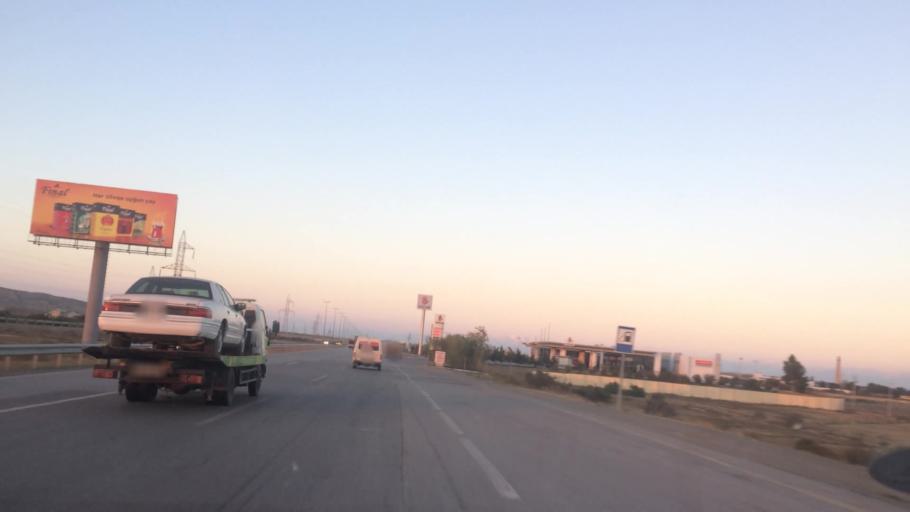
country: AZ
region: Baki
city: Qobustan
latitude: 39.9687
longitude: 49.4138
